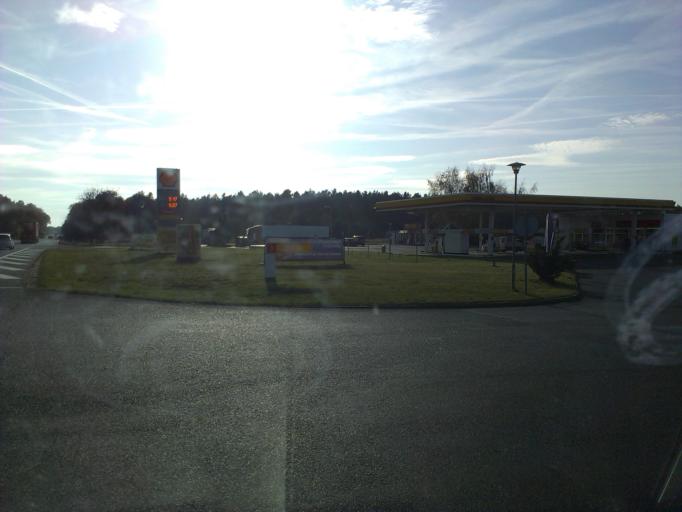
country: PL
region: Lubusz
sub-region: Powiat nowosolski
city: Nowe Miasteczko
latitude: 51.7193
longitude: 15.7293
